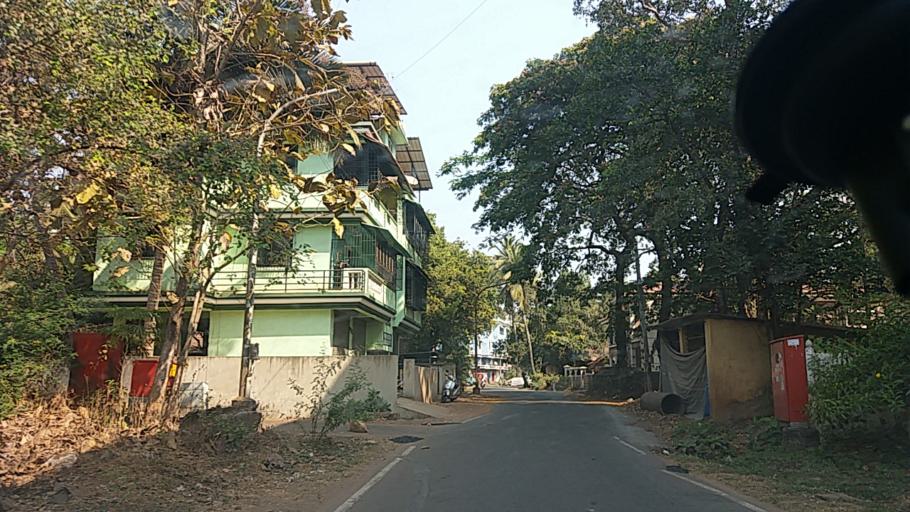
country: IN
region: Goa
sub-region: South Goa
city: Madgaon
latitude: 15.2830
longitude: 73.9540
